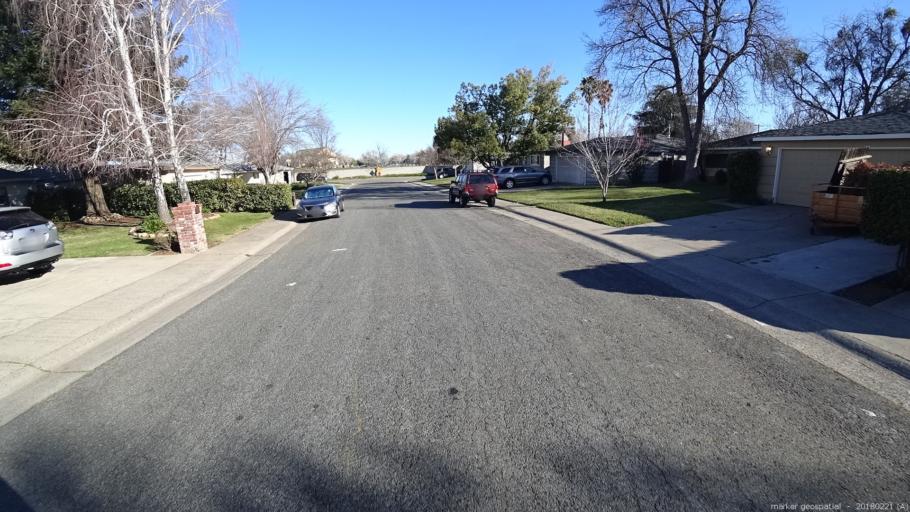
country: US
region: California
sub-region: Sacramento County
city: Orangevale
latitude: 38.6879
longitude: -121.2238
